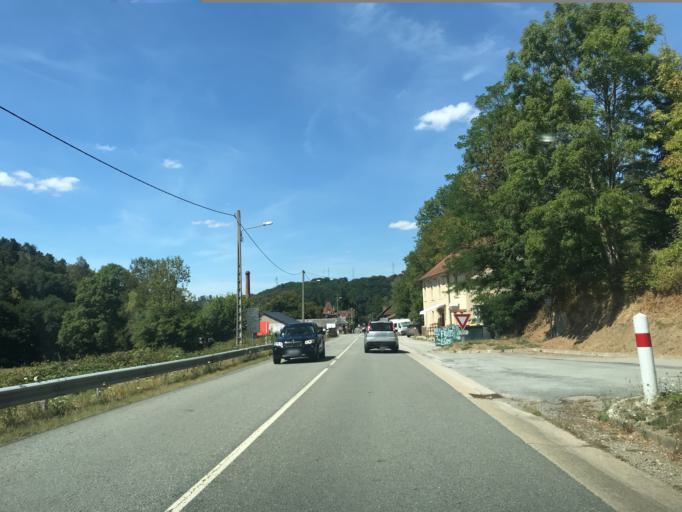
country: FR
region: Limousin
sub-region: Departement de la Creuse
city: Aubusson
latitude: 45.9222
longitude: 2.1923
